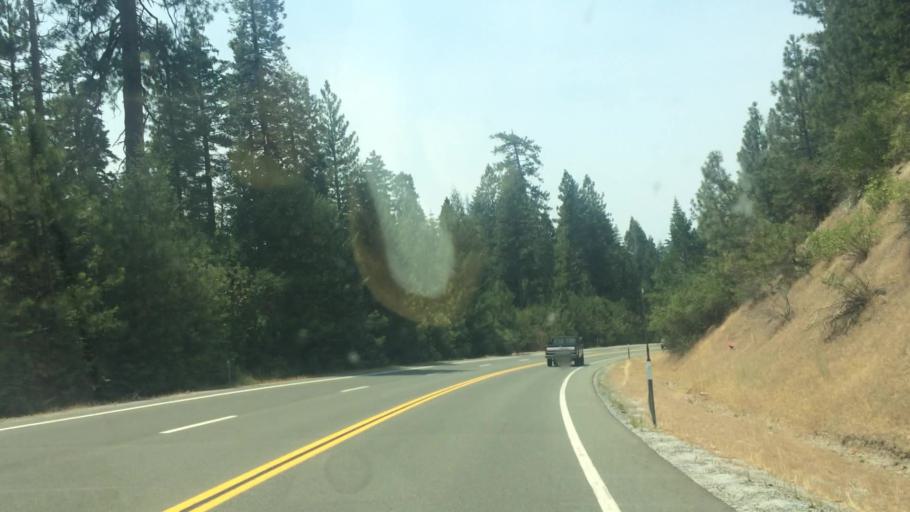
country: US
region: California
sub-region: Amador County
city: Pioneer
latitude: 38.5140
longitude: -120.4647
